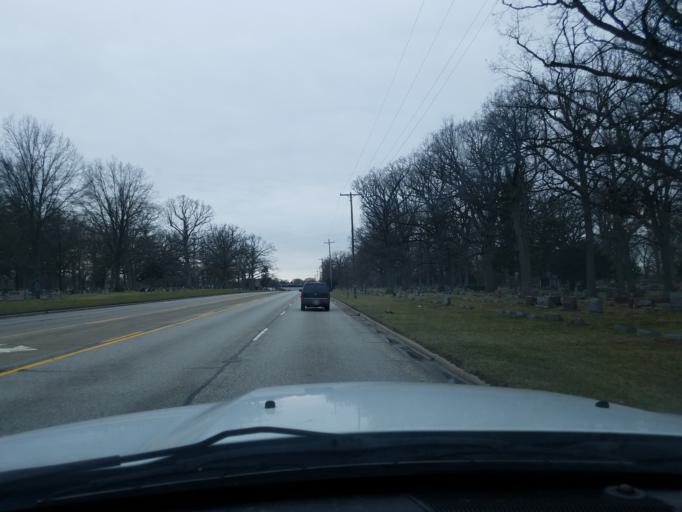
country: US
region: Indiana
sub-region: Tippecanoe County
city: Lafayette
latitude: 40.4485
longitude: -86.8599
